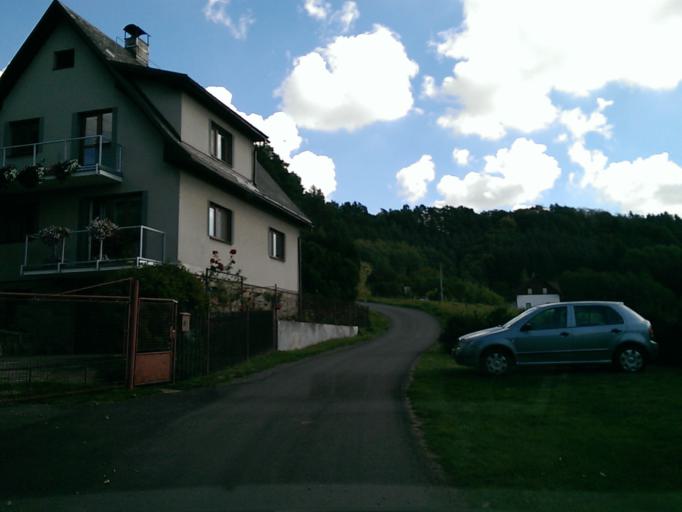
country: CZ
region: Liberecky
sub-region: Okres Semily
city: Turnov
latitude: 50.5455
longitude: 15.1277
